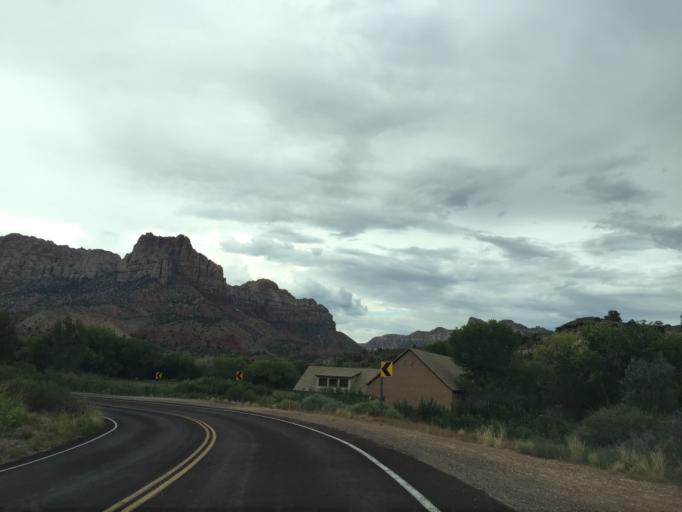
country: US
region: Utah
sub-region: Washington County
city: Hildale
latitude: 37.1608
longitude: -113.0189
